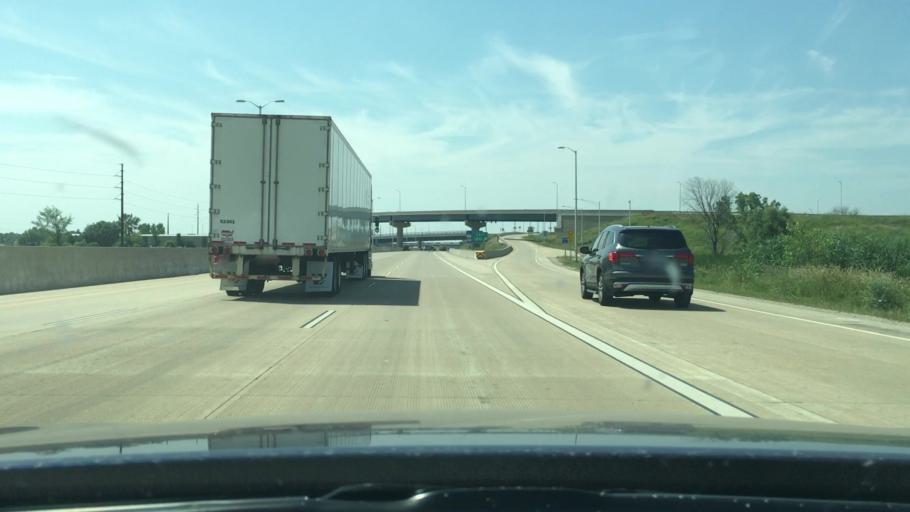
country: US
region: Wisconsin
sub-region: Winnebago County
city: Oshkosh
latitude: 44.0640
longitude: -88.5715
